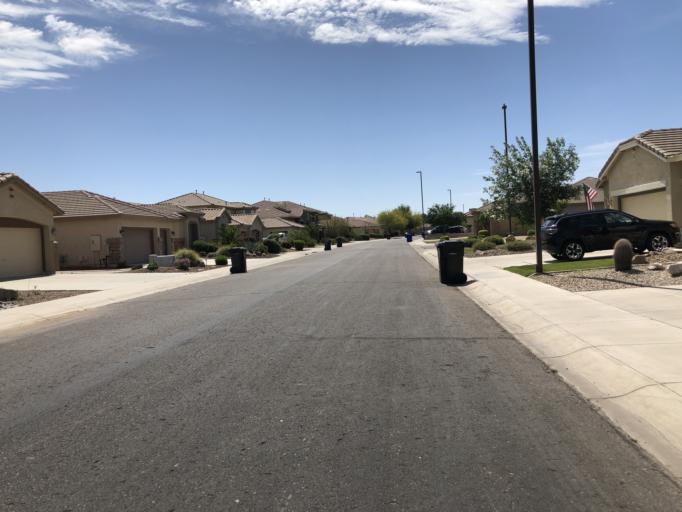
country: US
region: Arizona
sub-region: Maricopa County
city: Queen Creek
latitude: 33.2268
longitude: -111.7112
